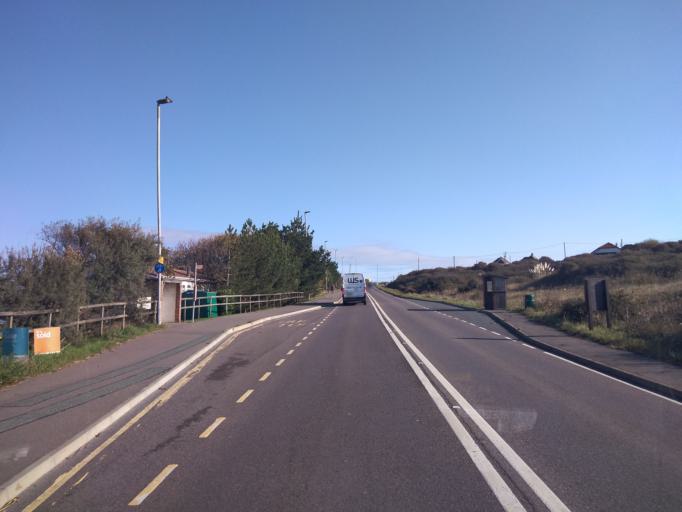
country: GB
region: England
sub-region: East Sussex
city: Peacehaven
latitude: 50.7888
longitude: 0.0233
